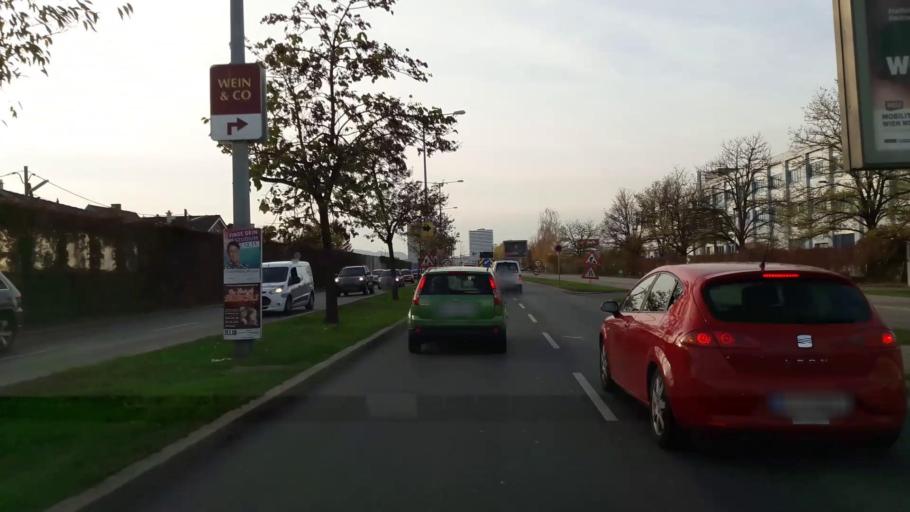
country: AT
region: Lower Austria
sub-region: Politischer Bezirk Wien-Umgebung
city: Gerasdorf bei Wien
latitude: 48.2598
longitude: 16.4737
